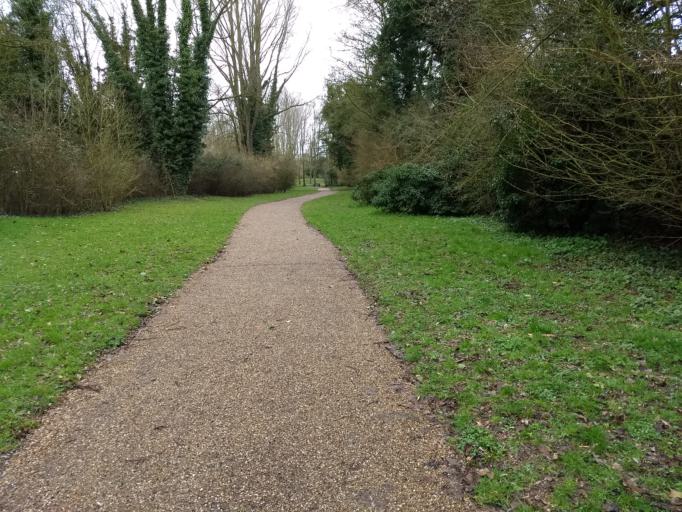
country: GB
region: England
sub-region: Milton Keynes
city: Stony Stratford
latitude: 52.0619
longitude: -0.8489
